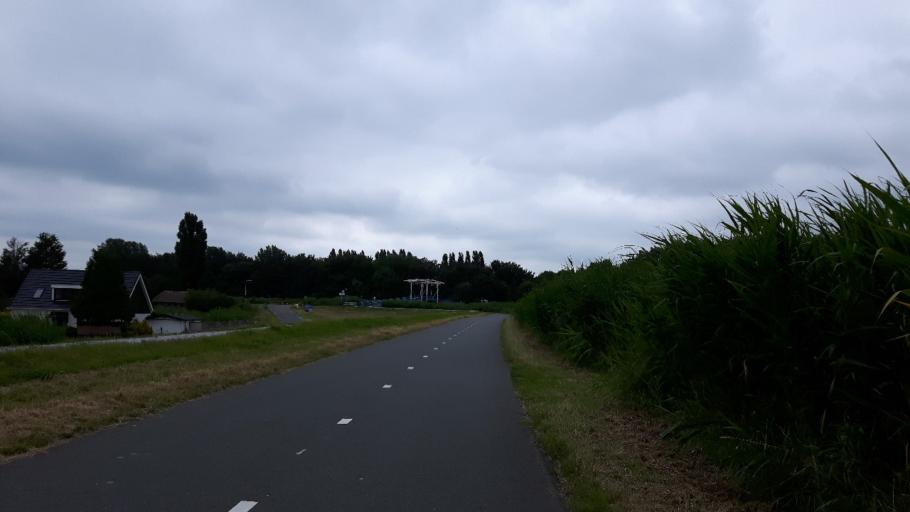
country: NL
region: South Holland
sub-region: Gemeente Lansingerland
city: Bleiswijk
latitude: 51.9920
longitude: 4.5487
